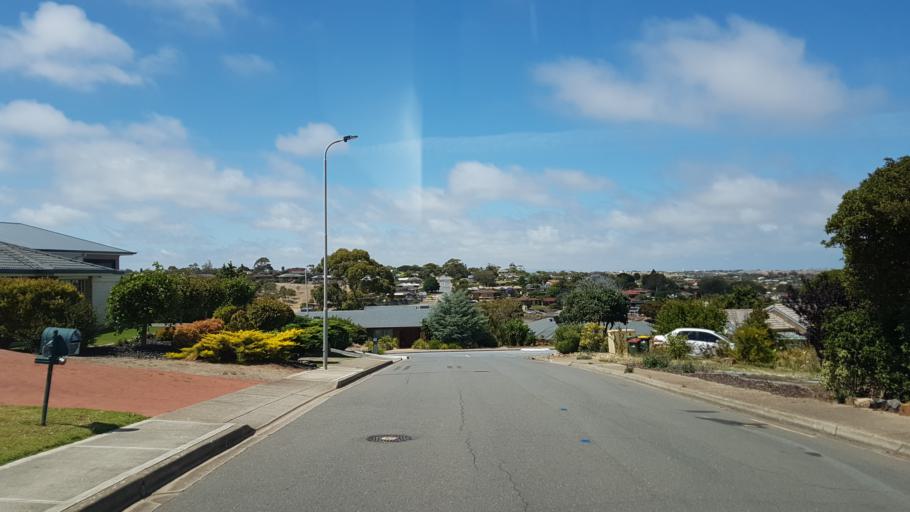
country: AU
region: South Australia
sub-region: Marion
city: Marino
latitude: -35.0690
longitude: 138.5090
